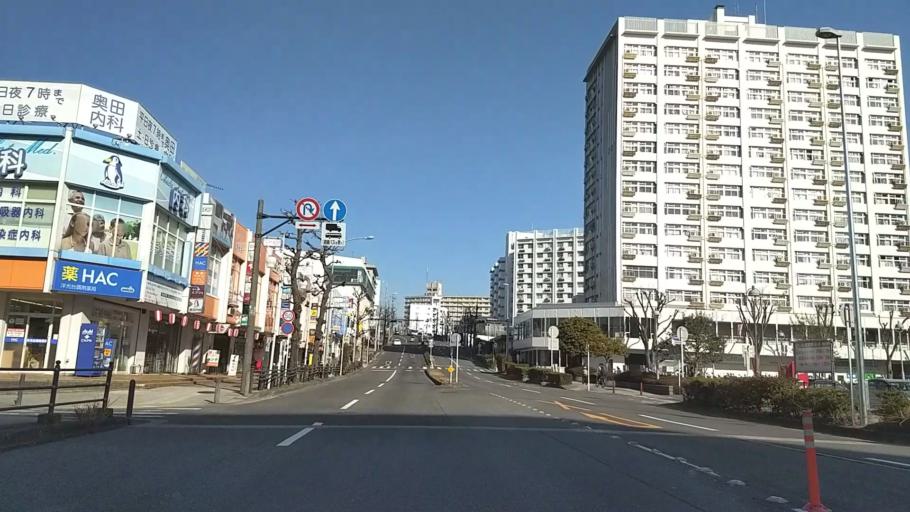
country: JP
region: Kanagawa
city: Kamakura
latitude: 35.3783
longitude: 139.5956
